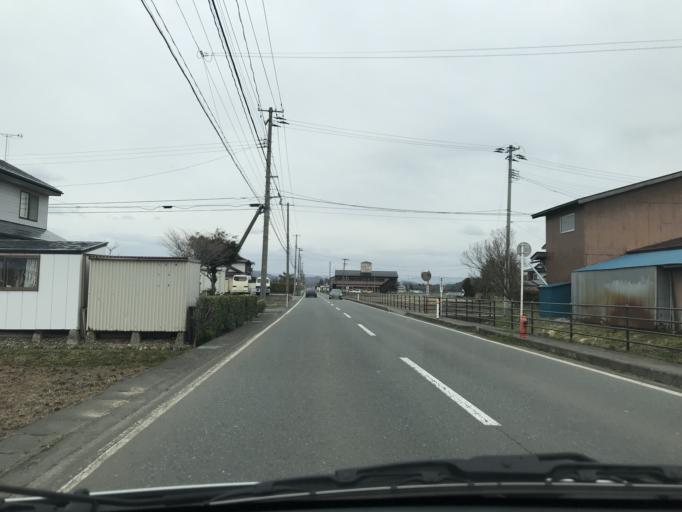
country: JP
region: Iwate
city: Kitakami
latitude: 39.2816
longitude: 141.0688
